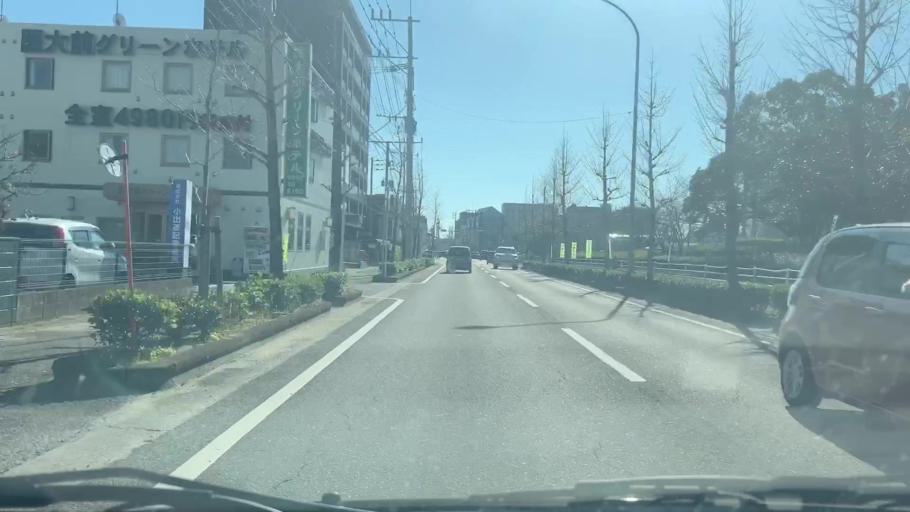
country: JP
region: Saga Prefecture
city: Saga-shi
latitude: 33.2846
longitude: 130.2685
